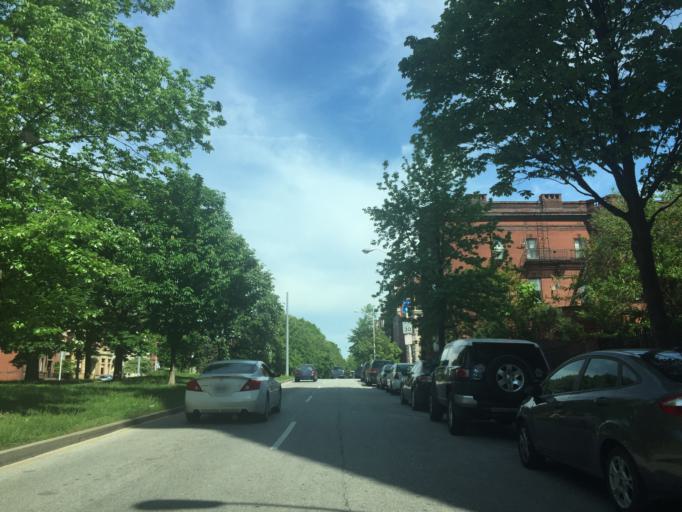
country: US
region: Maryland
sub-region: City of Baltimore
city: Baltimore
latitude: 39.3074
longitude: -76.6301
